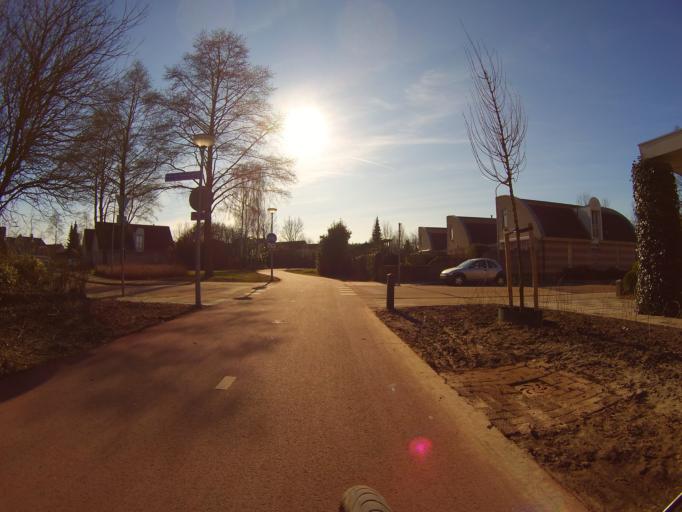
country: NL
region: Gelderland
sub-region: Gemeente Nijkerk
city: Nijkerk
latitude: 52.2172
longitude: 5.4725
